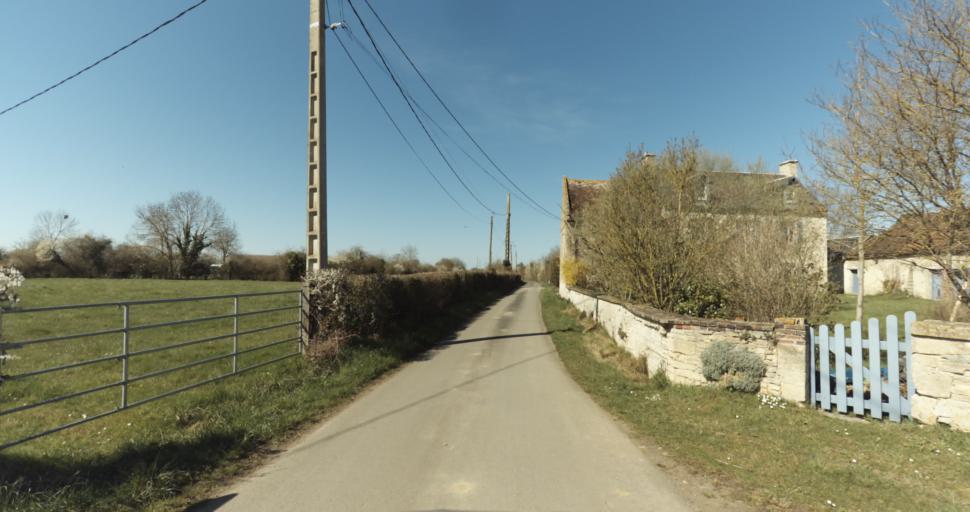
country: FR
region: Lower Normandy
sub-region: Departement du Calvados
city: Saint-Pierre-sur-Dives
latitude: 49.0503
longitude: -0.0320
